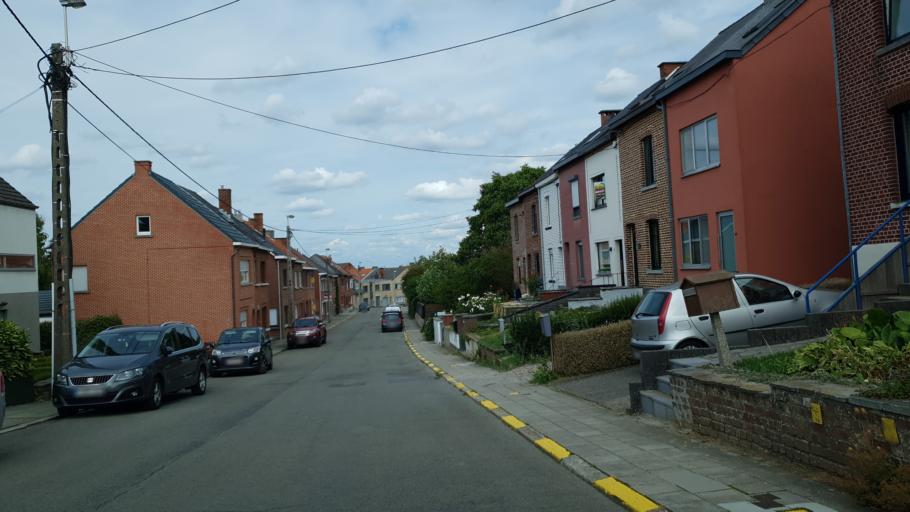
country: BE
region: Flanders
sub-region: Provincie Vlaams-Brabant
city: Herent
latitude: 50.8974
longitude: 4.6813
